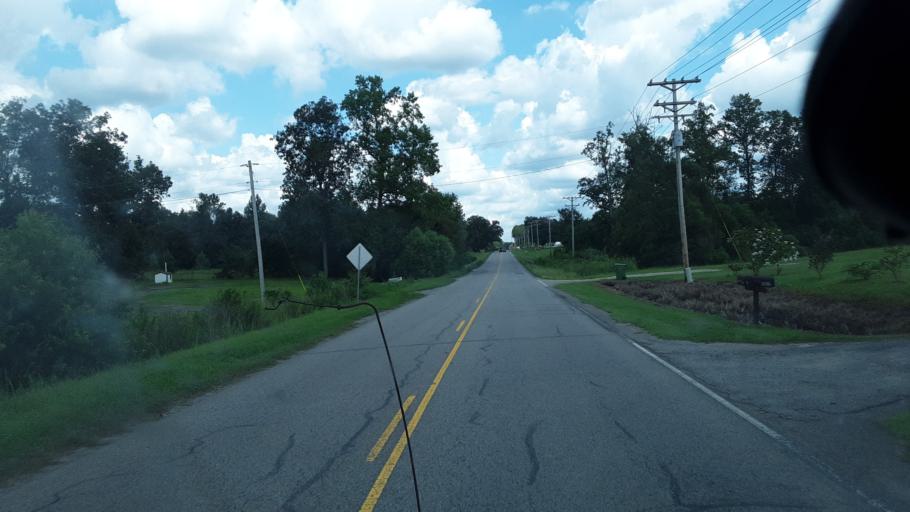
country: US
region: South Carolina
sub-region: Williamsburg County
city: Andrews
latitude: 33.5058
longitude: -79.5195
